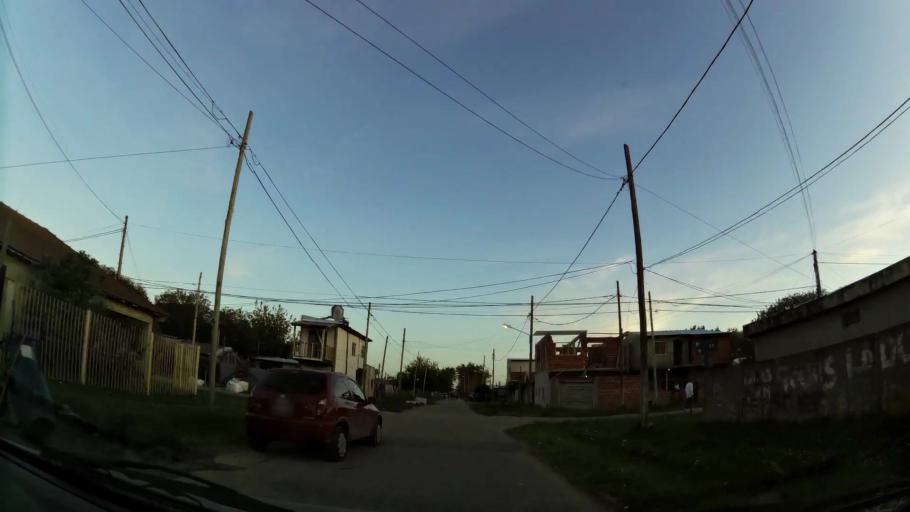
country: AR
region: Buenos Aires
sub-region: Partido de Quilmes
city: Quilmes
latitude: -34.7895
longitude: -58.2252
